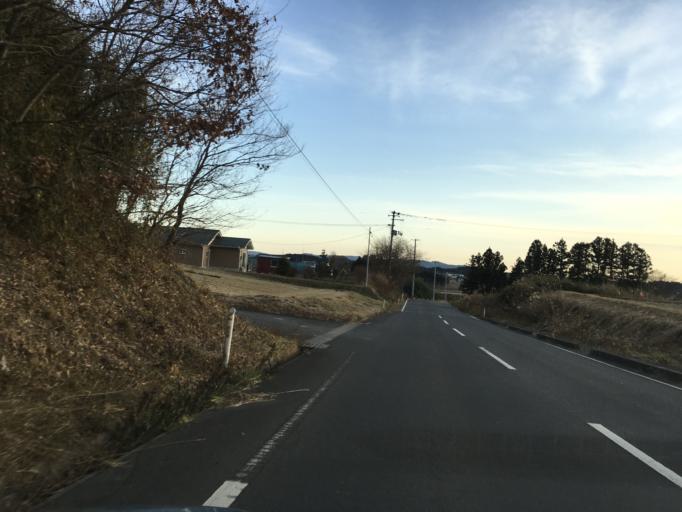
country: JP
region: Miyagi
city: Kogota
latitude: 38.6933
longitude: 141.0954
